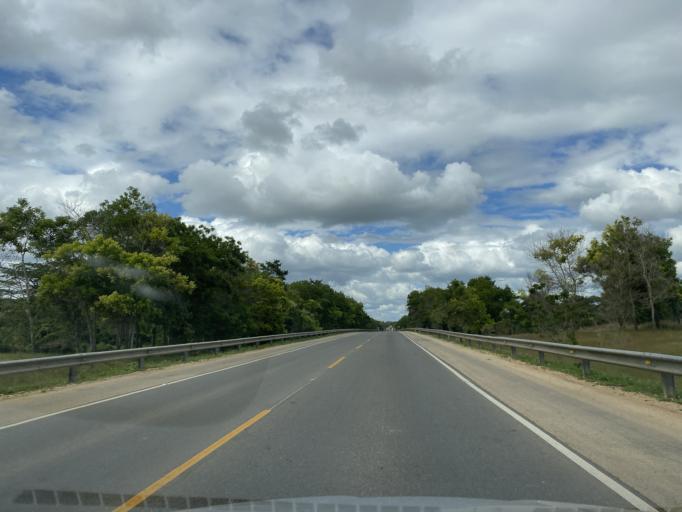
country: DO
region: Santo Domingo
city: Guerra
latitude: 18.5360
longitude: -69.7550
